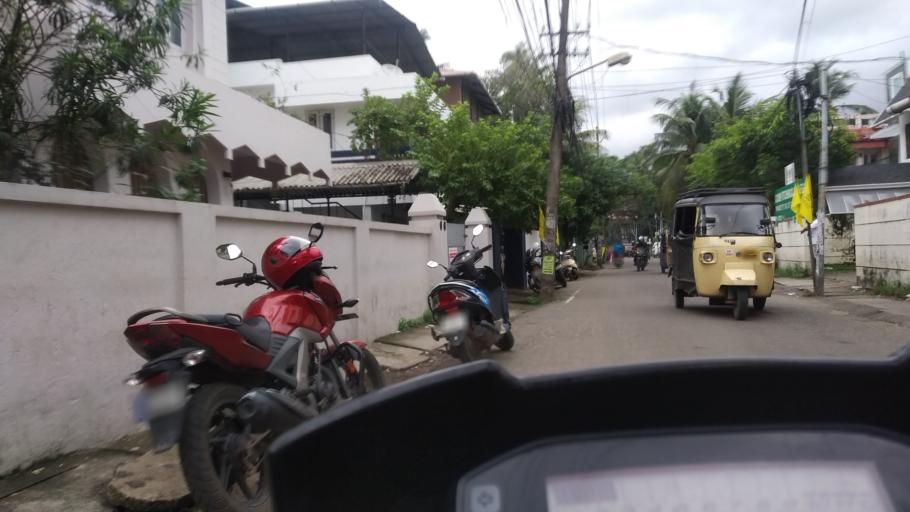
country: IN
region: Kerala
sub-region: Ernakulam
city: Cochin
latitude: 9.9937
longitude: 76.2957
